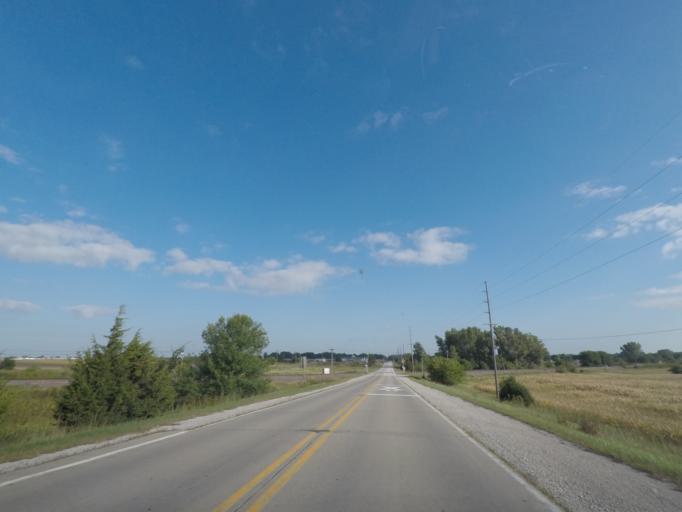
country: US
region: Iowa
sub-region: Story County
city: Nevada
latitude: 42.0069
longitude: -93.4629
